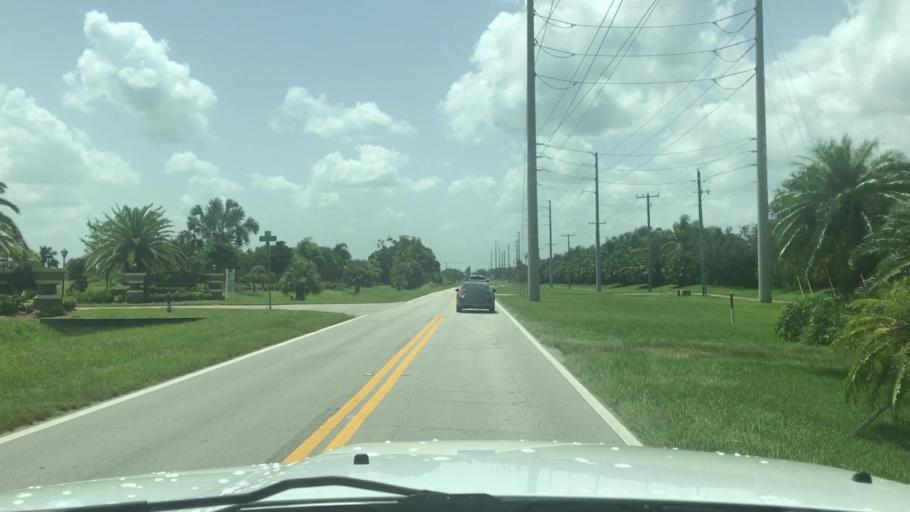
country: US
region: Florida
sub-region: Indian River County
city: Vero Beach South
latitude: 27.6241
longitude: -80.4395
